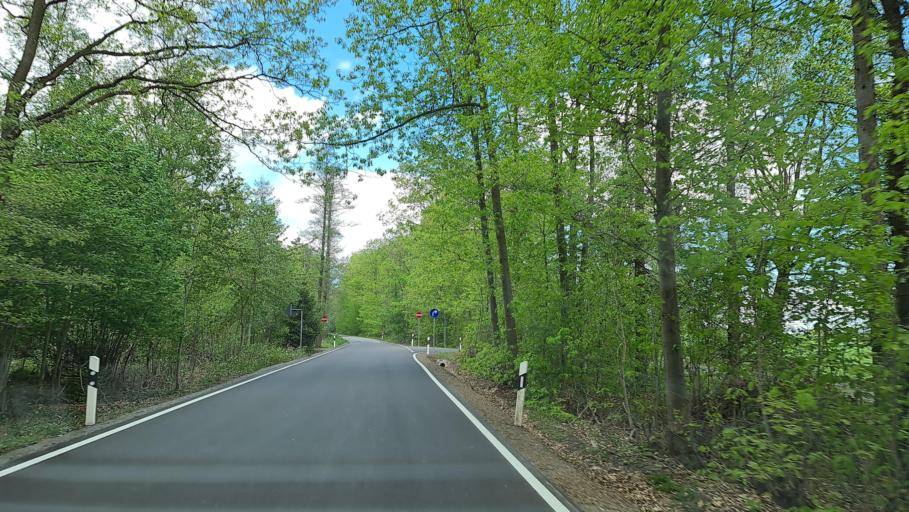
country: DE
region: Saxony
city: Hilbersdorf
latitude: 50.8396
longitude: 12.9887
